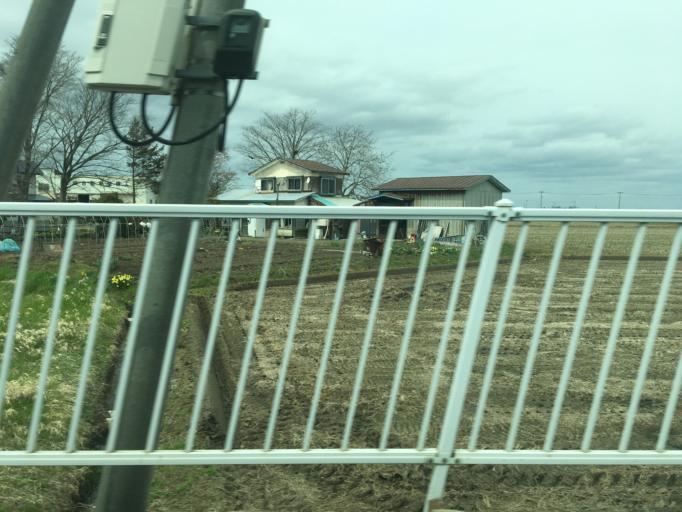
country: JP
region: Aomori
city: Shimokizukuri
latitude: 40.7874
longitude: 140.3644
